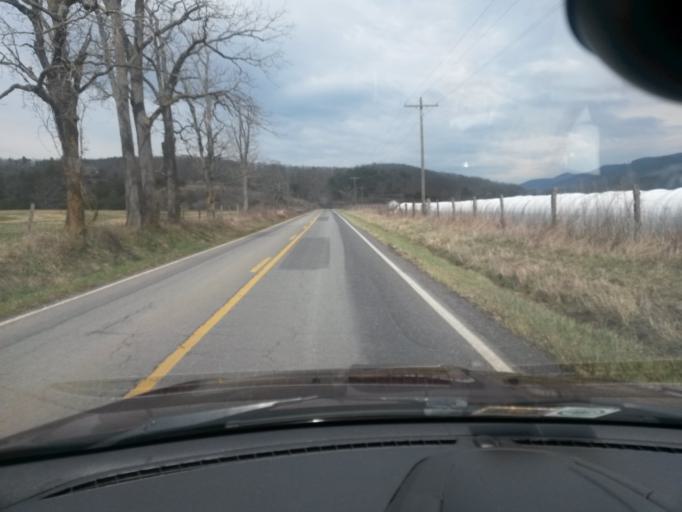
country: US
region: Virginia
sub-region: Bath County
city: Warm Springs
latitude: 38.2324
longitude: -79.6980
